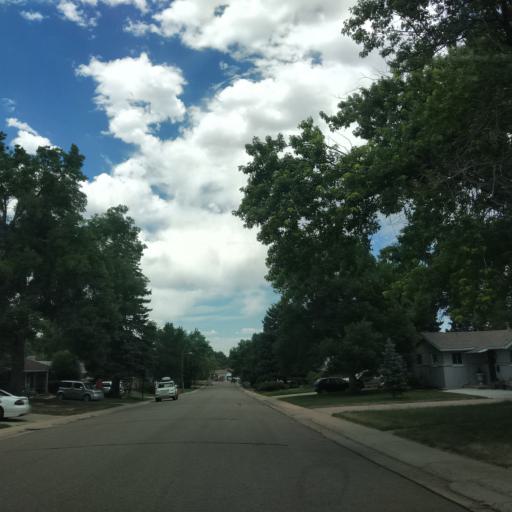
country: US
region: Colorado
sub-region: Jefferson County
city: Lakewood
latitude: 39.6863
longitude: -105.0871
